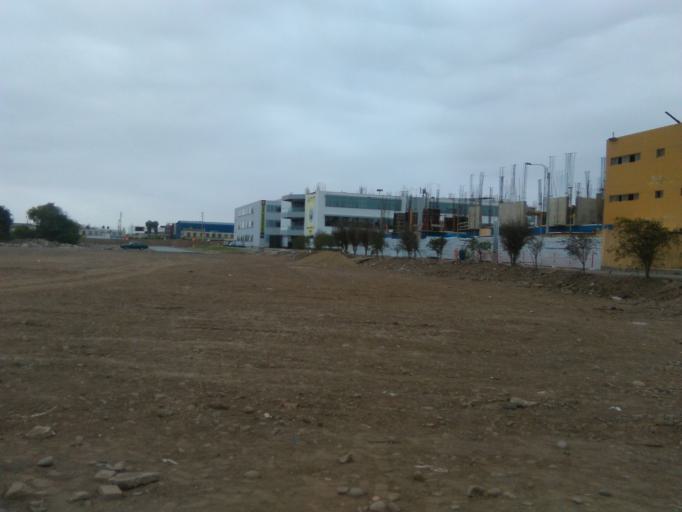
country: PE
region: Callao
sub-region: Callao
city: Callao
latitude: -12.0536
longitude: -77.0861
